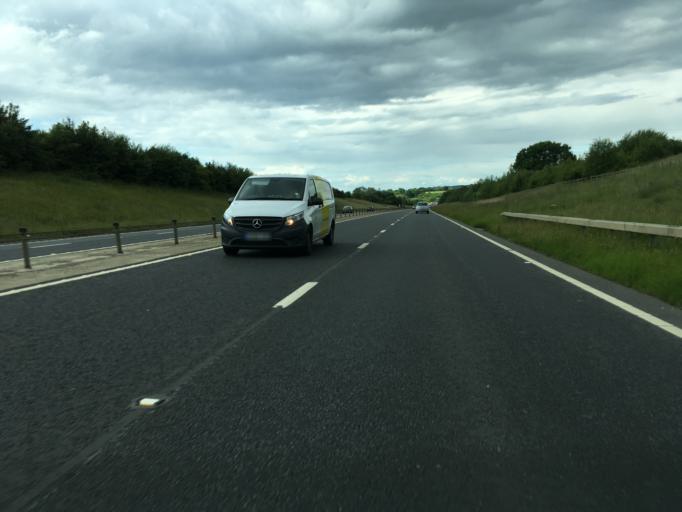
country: GB
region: England
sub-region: Central Bedfordshire
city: Leighton Buzzard
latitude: 51.9152
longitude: -0.7005
